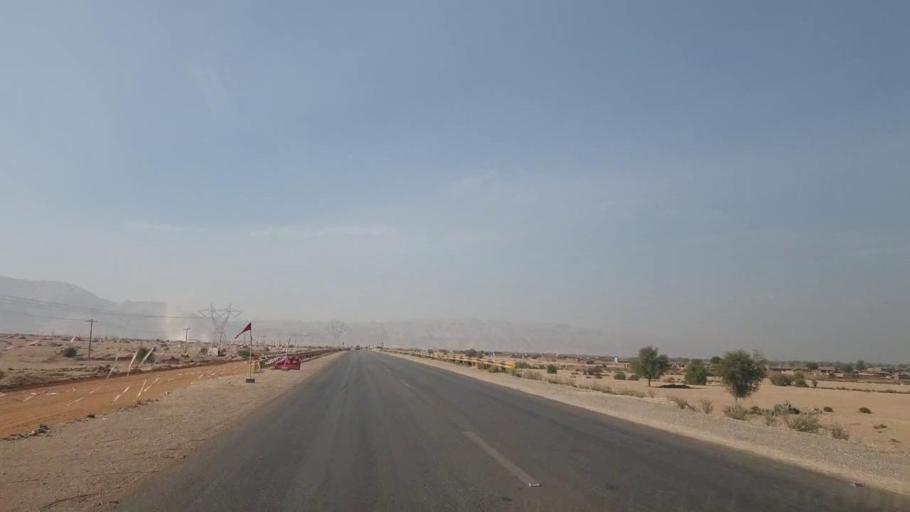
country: PK
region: Sindh
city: Sehwan
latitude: 26.2046
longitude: 67.9324
